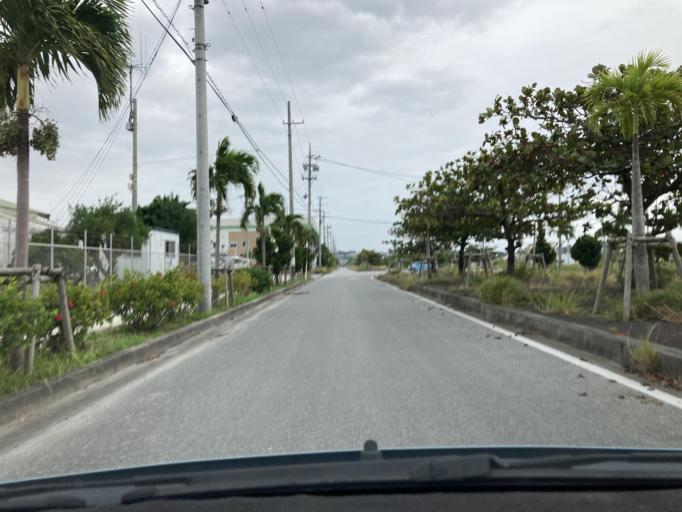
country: JP
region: Okinawa
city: Itoman
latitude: 26.1355
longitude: 127.6520
